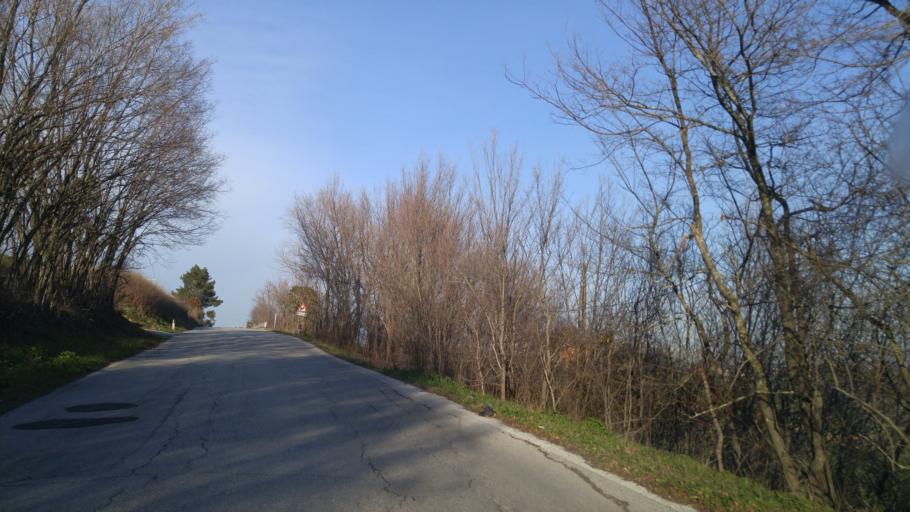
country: IT
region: The Marches
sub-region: Provincia di Pesaro e Urbino
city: Montemaggiore al Metauro
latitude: 43.7395
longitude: 12.9561
